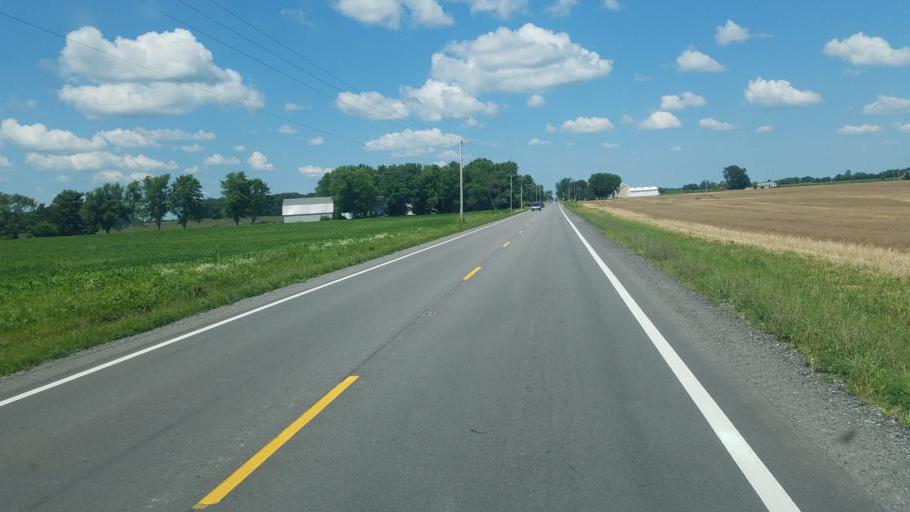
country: US
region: Ohio
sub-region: Marion County
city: Marion
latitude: 40.6317
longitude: -83.0252
